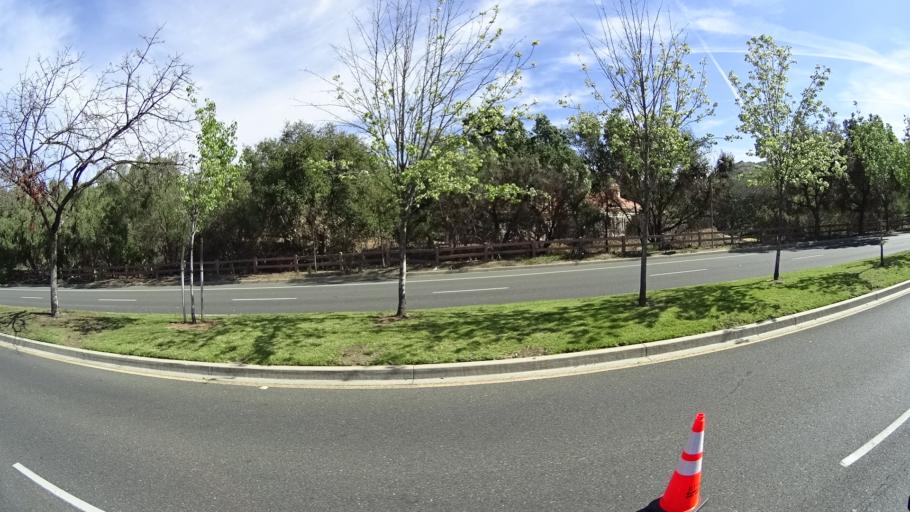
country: US
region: California
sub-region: Ventura County
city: Thousand Oaks
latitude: 34.1989
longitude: -118.8123
